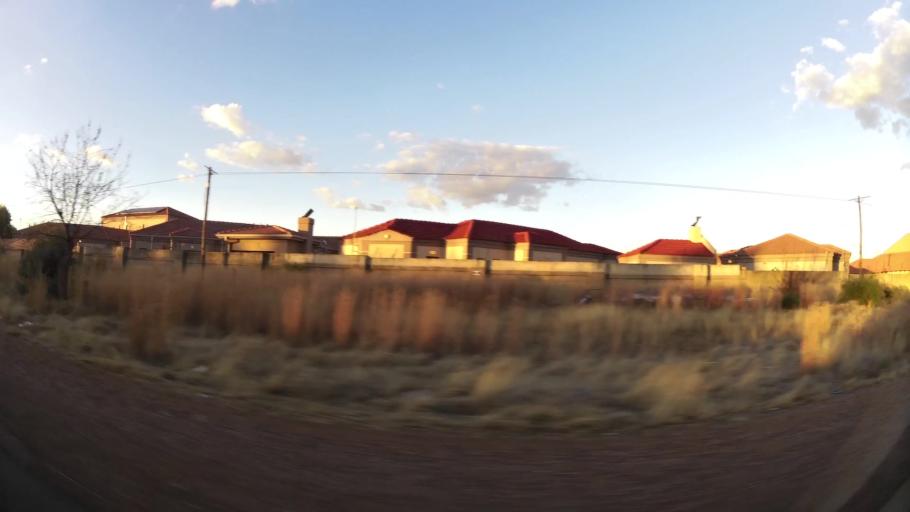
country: ZA
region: North-West
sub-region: Dr Kenneth Kaunda District Municipality
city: Potchefstroom
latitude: -26.7256
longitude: 27.1168
